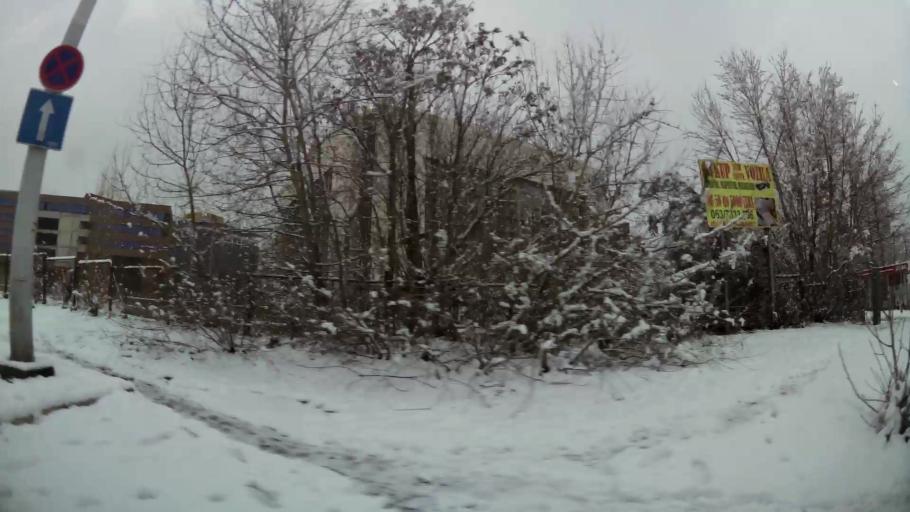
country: RS
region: Central Serbia
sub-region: Belgrade
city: Novi Beograd
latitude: 44.8120
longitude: 20.4384
